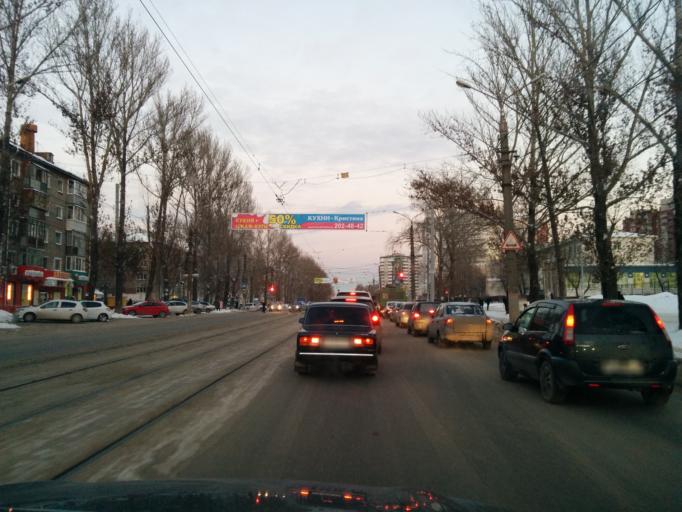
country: RU
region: Perm
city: Perm
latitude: 57.9800
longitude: 56.1920
